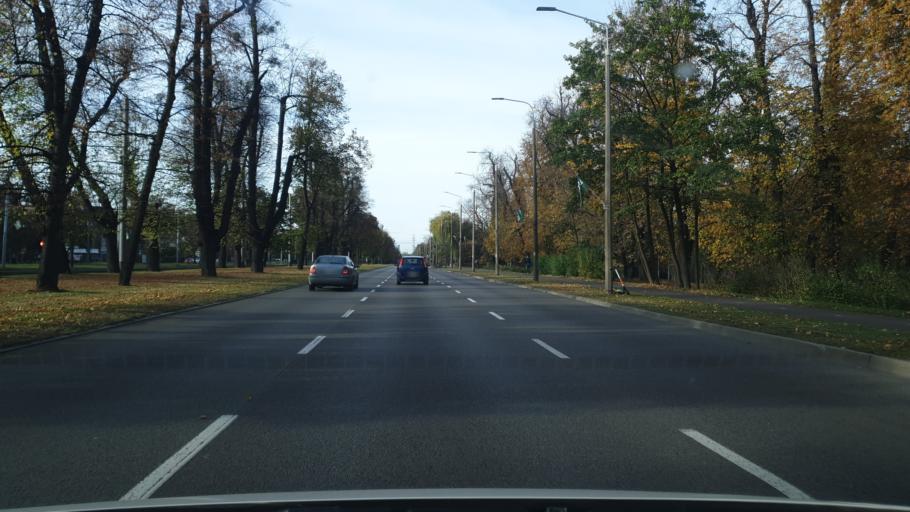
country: PL
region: Pomeranian Voivodeship
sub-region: Gdansk
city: Gdansk
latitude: 54.3654
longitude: 18.6364
